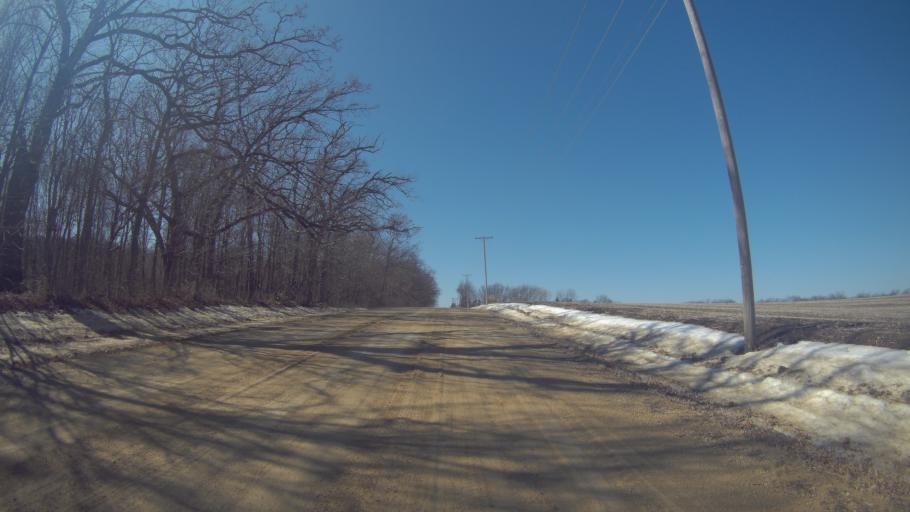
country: US
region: Illinois
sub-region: Winnebago County
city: Lake Summerset
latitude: 42.4004
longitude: -89.4532
